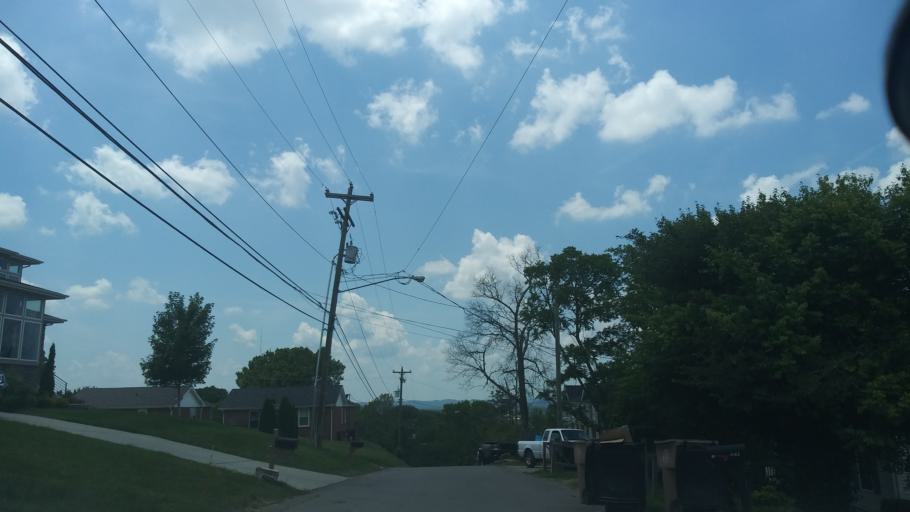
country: US
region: Tennessee
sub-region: Davidson County
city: Nashville
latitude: 36.1496
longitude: -86.8257
